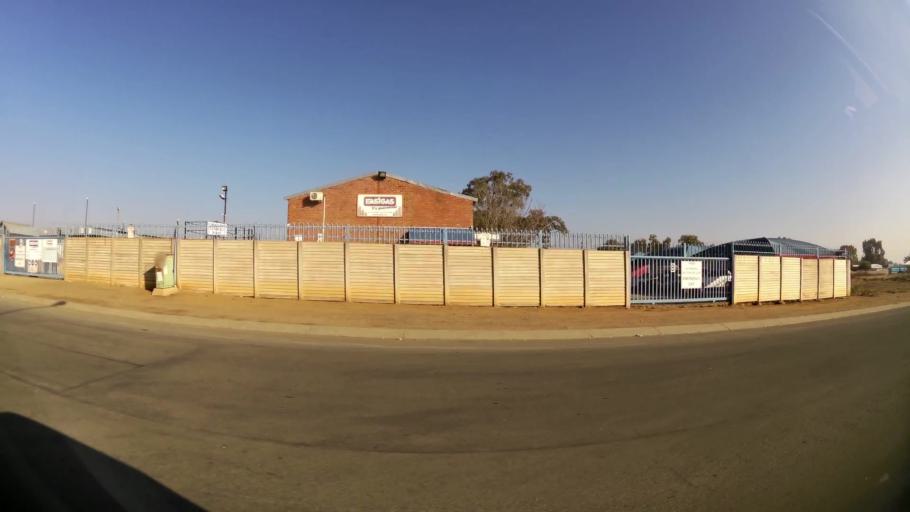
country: ZA
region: Orange Free State
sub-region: Mangaung Metropolitan Municipality
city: Bloemfontein
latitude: -29.1310
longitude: 26.2658
